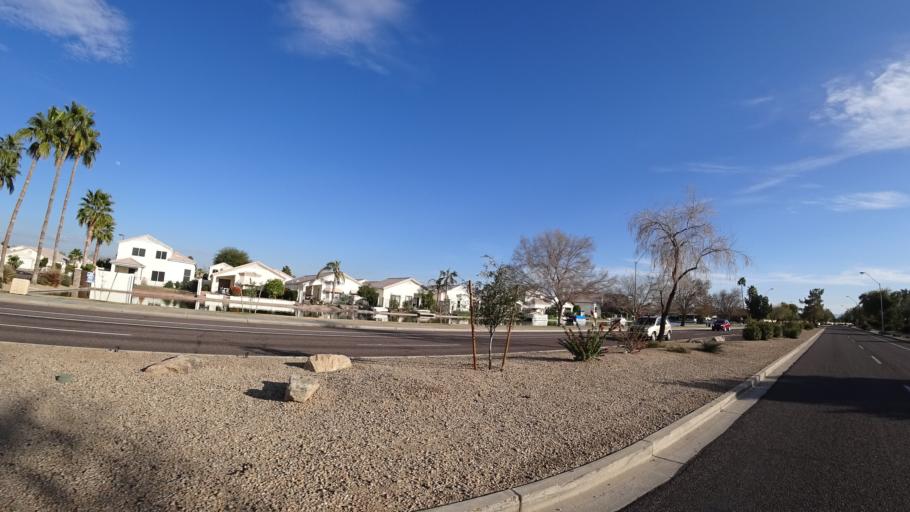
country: US
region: Arizona
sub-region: Maricopa County
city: Sun City
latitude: 33.6162
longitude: -112.2536
